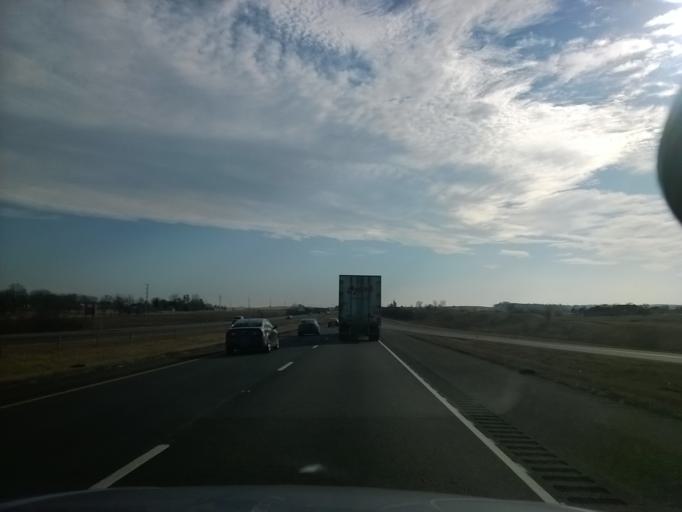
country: US
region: Indiana
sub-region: Johnson County
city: Edinburgh
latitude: 39.3602
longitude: -85.9426
